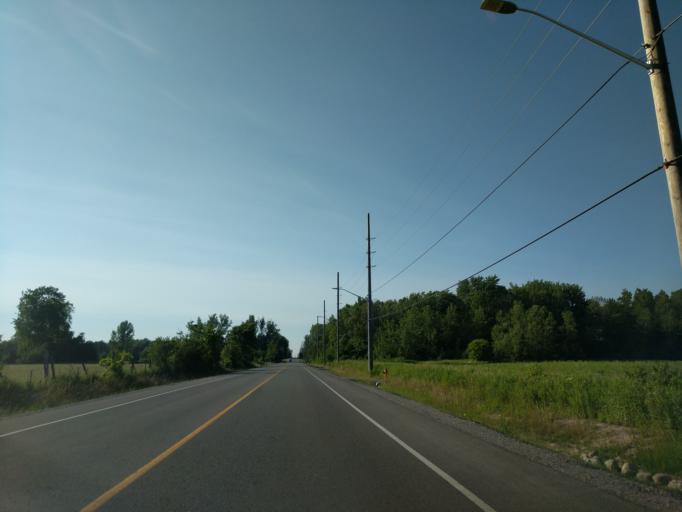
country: CA
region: Ontario
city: Oshawa
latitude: 43.9317
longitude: -78.9105
